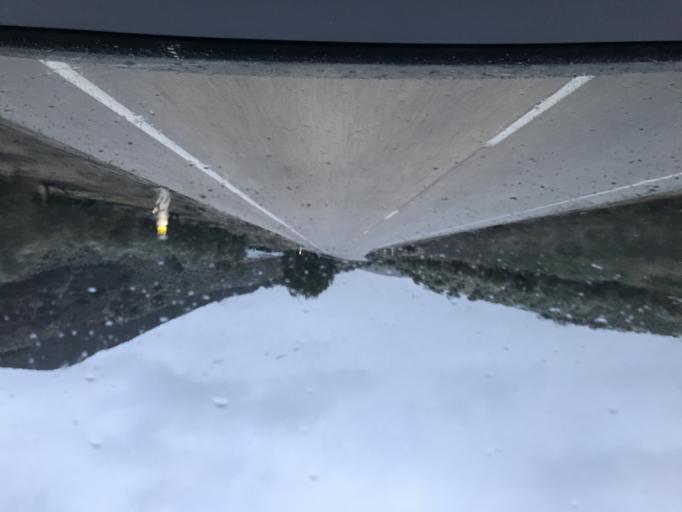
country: ES
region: Andalusia
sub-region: Provincia de Granada
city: Campotejar
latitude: 37.4596
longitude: -3.6072
